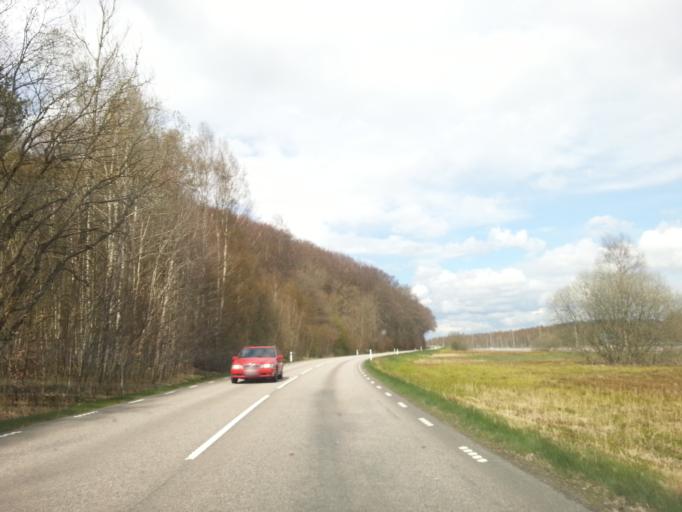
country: SE
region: Vaestra Goetaland
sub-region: Ale Kommun
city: Surte
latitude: 57.8357
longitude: 12.0045
